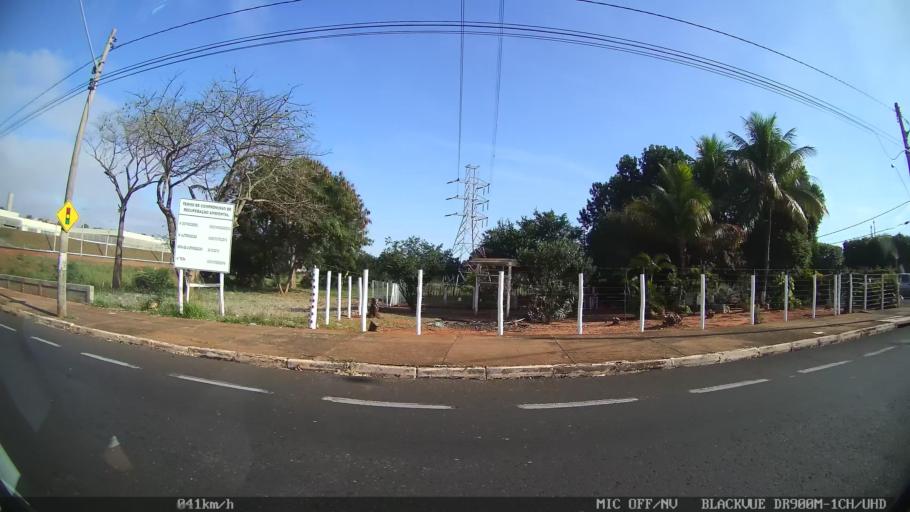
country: BR
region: Sao Paulo
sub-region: Sao Jose Do Rio Preto
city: Sao Jose do Rio Preto
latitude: -20.7888
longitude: -49.4120
